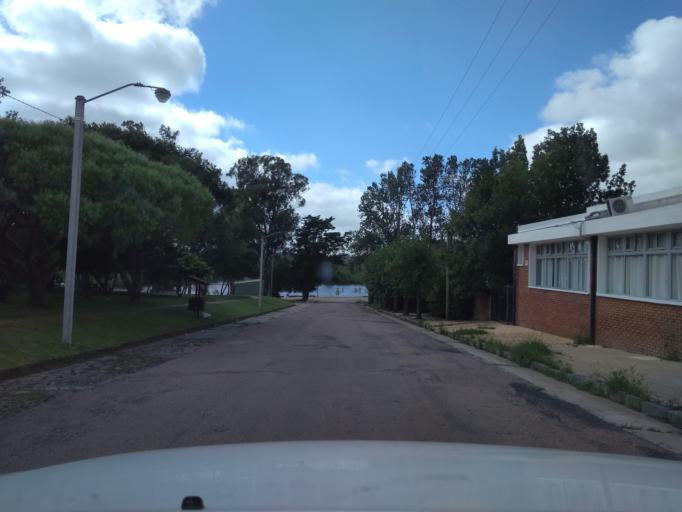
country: UY
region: Florida
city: Florida
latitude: -34.1011
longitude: -56.2045
